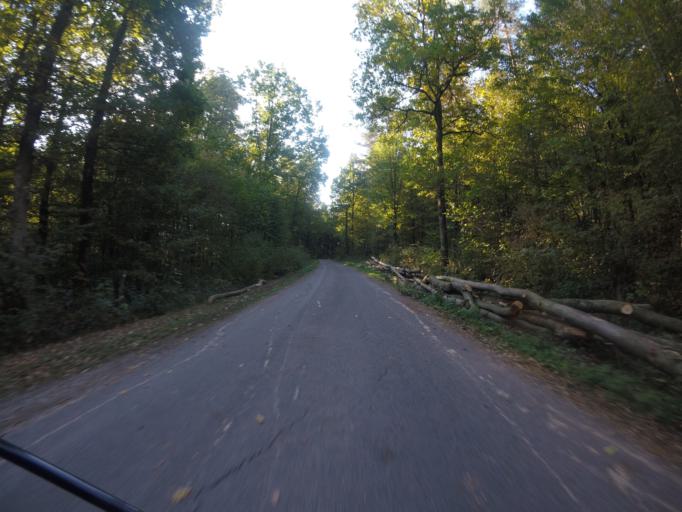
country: DE
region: Baden-Wuerttemberg
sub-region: Regierungsbezirk Stuttgart
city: Oppenweiler
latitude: 48.9934
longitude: 9.4278
